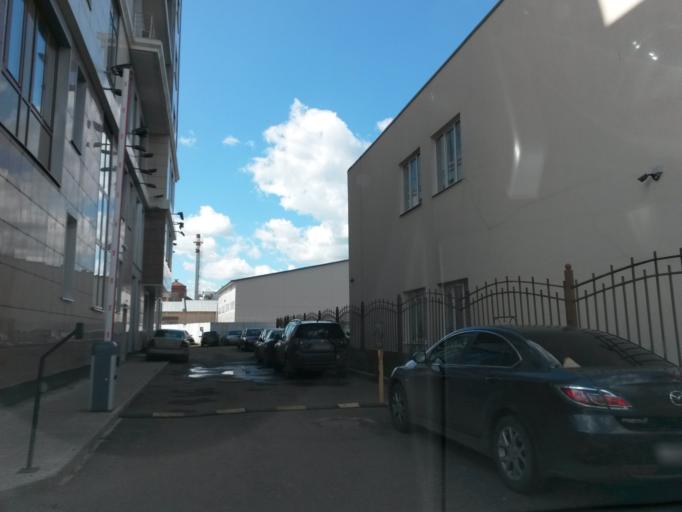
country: RU
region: Jaroslavl
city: Yaroslavl
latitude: 57.6368
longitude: 39.8768
